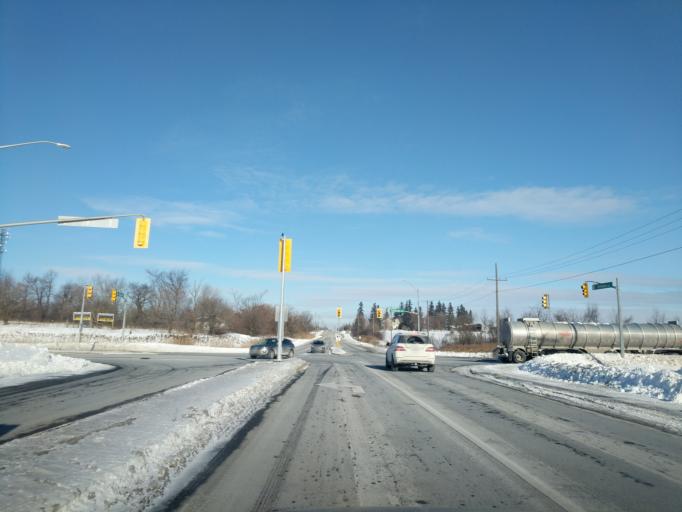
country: CA
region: Ontario
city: Pickering
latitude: 43.8587
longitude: -79.1545
